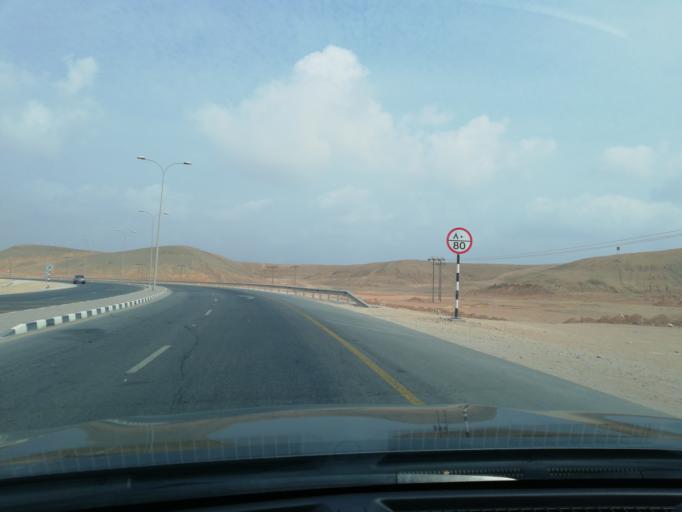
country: OM
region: Zufar
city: Salalah
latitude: 16.9497
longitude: 53.9865
